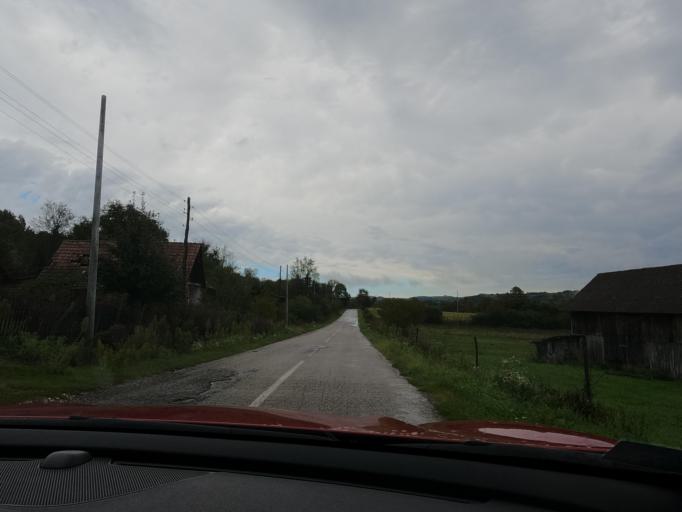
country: HR
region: Sisacko-Moslavacka
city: Glina
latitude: 45.3082
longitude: 16.1836
